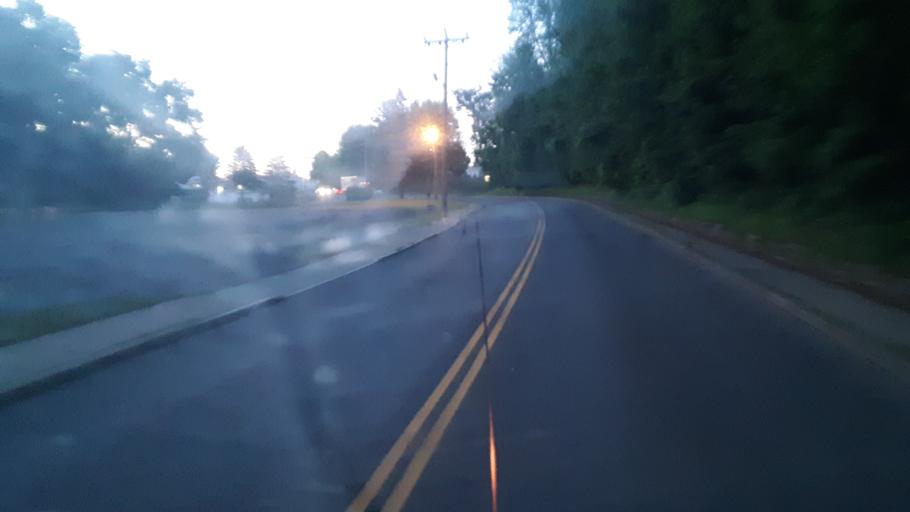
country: US
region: New York
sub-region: Montgomery County
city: Amsterdam
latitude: 42.9387
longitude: -74.1842
